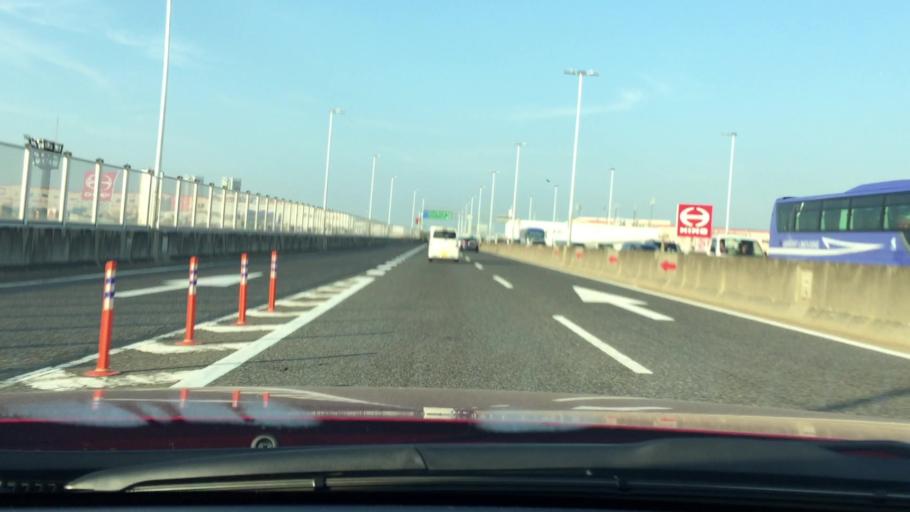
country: JP
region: Osaka
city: Takaishi
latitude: 34.5166
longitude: 135.4163
